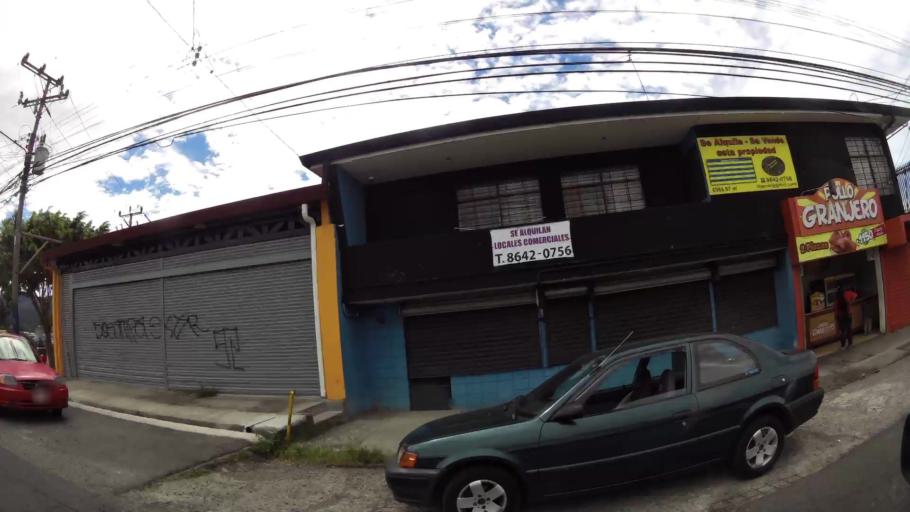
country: CR
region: San Jose
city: San Rafael Arriba
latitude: 9.8900
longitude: -84.0720
